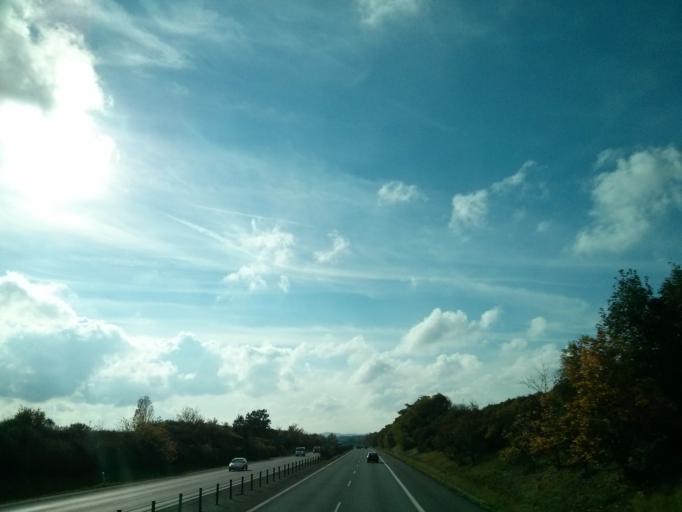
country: CZ
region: Central Bohemia
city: Rudna
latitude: 50.0447
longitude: 14.2442
